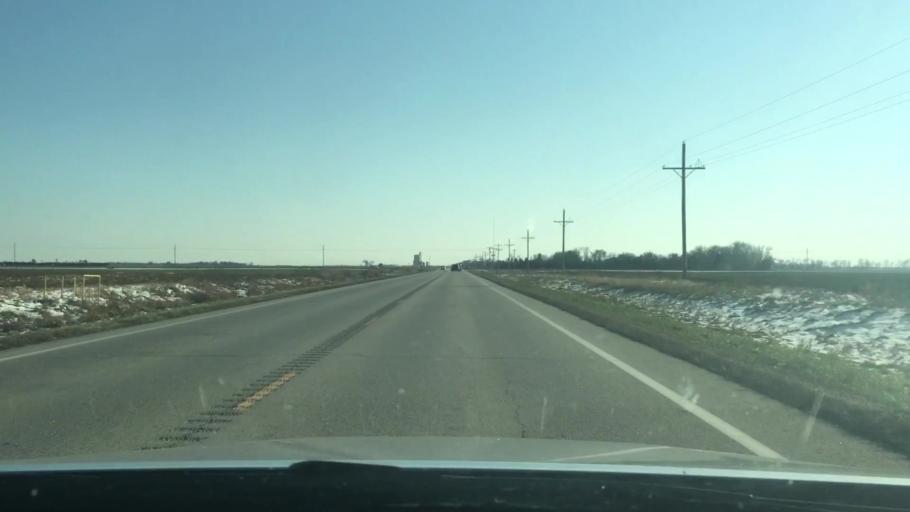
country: US
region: Kansas
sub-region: Rice County
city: Lyons
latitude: 38.2933
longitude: -98.2019
